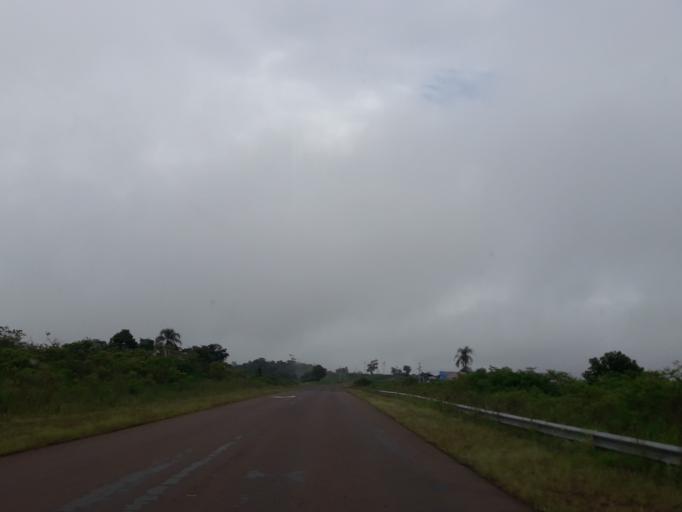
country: AR
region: Misiones
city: Bernardo de Irigoyen
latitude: -26.4121
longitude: -53.8235
